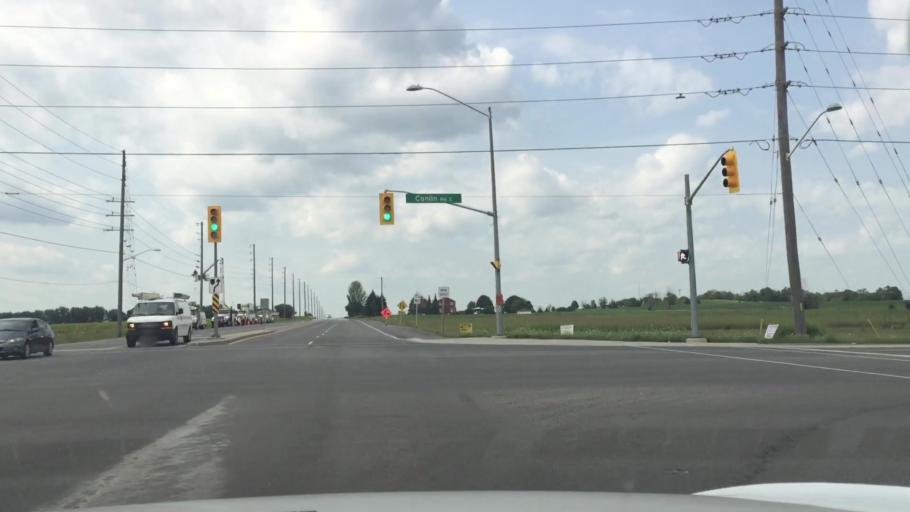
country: CA
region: Ontario
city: Oshawa
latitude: 43.9568
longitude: -78.8570
